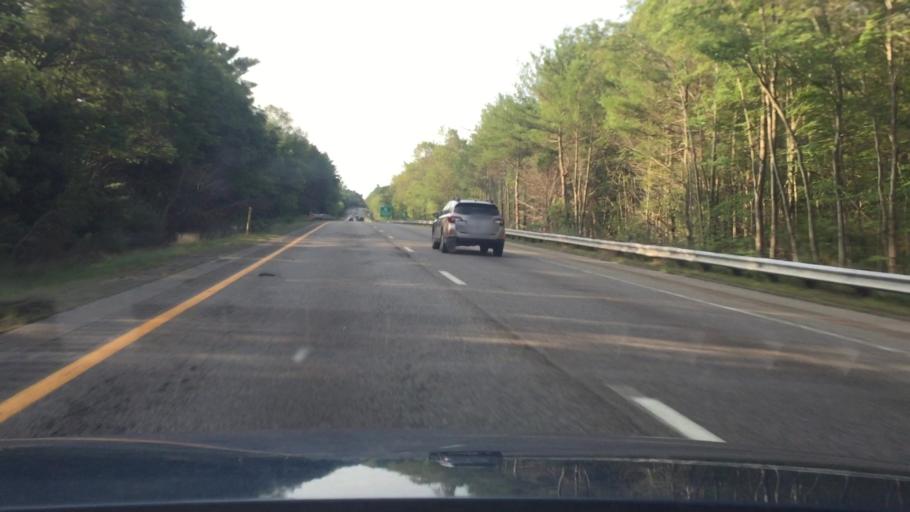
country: US
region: Massachusetts
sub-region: Plymouth County
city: Marshfield
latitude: 42.0740
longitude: -70.7345
